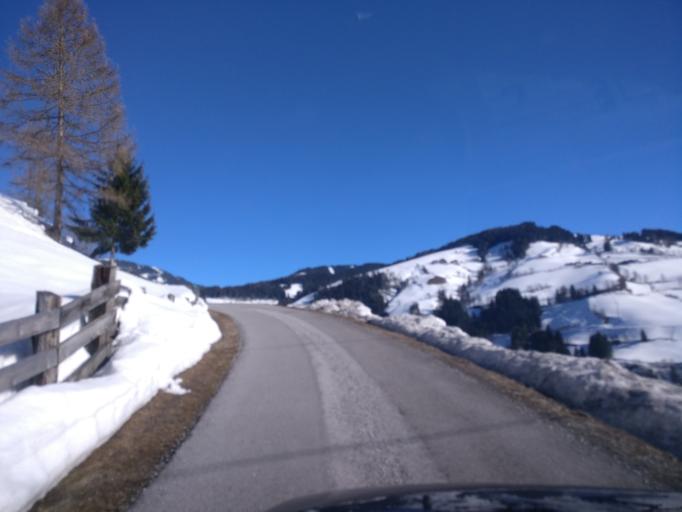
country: AT
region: Salzburg
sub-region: Politischer Bezirk Sankt Johann im Pongau
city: Wagrain
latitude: 47.3387
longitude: 13.2599
